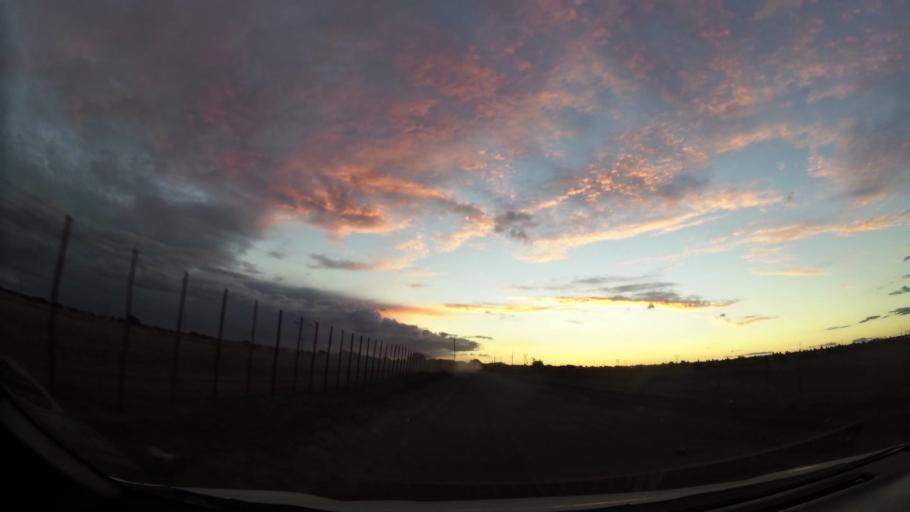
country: ZA
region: Limpopo
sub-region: Capricorn District Municipality
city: Polokwane
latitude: -23.7328
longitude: 29.4101
